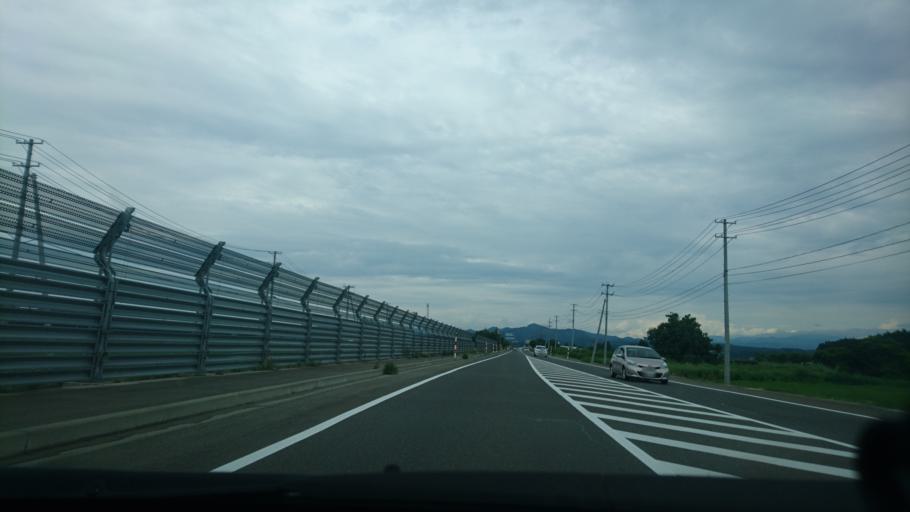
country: JP
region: Akita
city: Omagari
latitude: 39.5181
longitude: 140.3770
